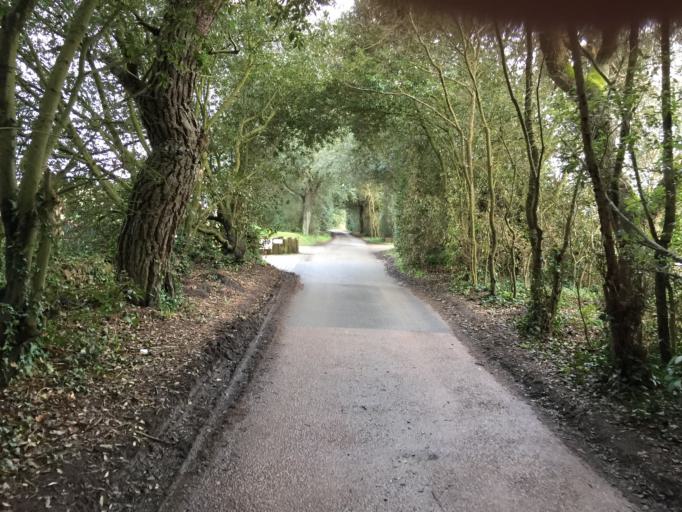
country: JE
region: St Helier
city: Saint Helier
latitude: 49.1861
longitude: -2.2150
